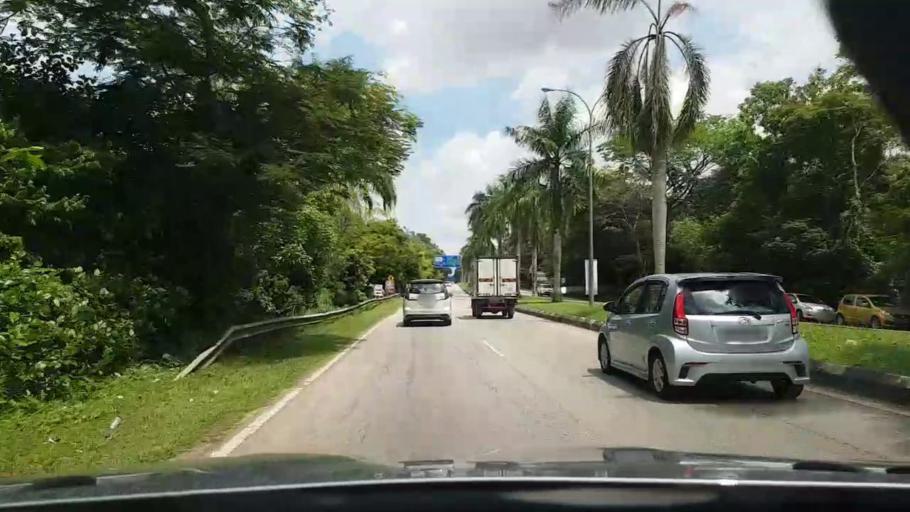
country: MY
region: Pahang
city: Kuantan
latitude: 3.8292
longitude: 103.2980
